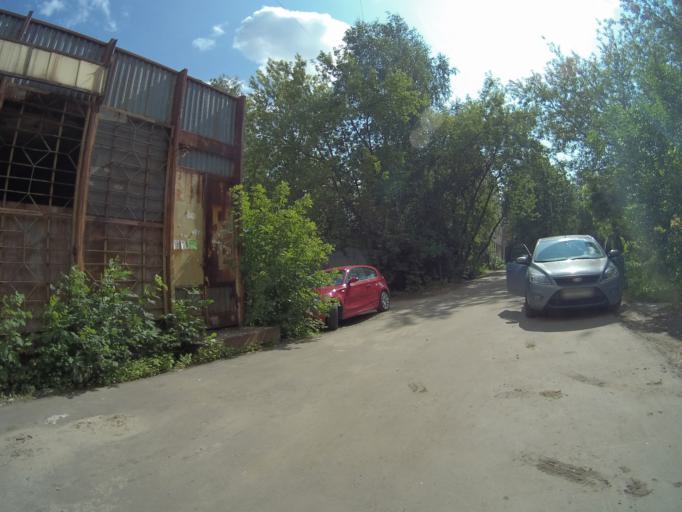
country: RU
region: Vladimir
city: Vladimir
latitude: 56.1415
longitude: 40.4020
